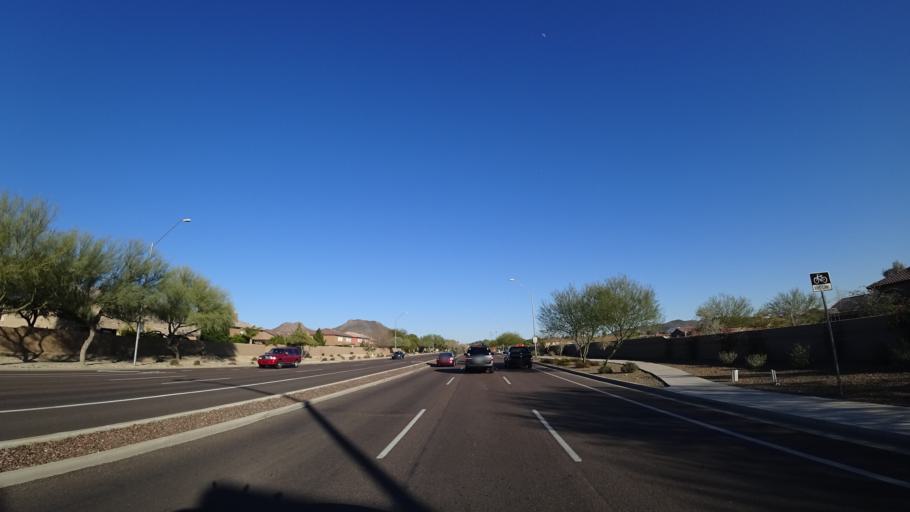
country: US
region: Arizona
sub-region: Maricopa County
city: Sun City
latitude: 33.7107
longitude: -112.2181
